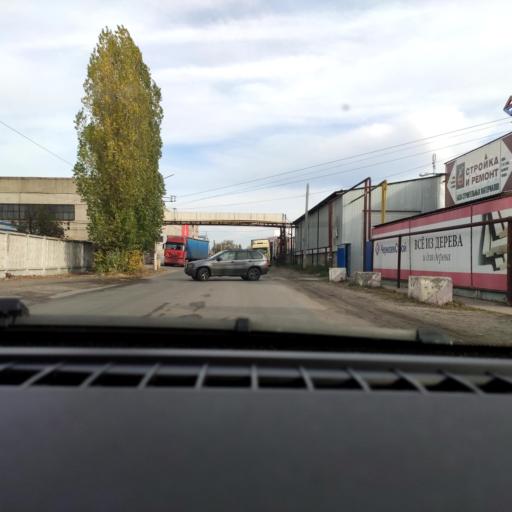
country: RU
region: Voronezj
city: Voronezh
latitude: 51.6546
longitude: 39.2837
